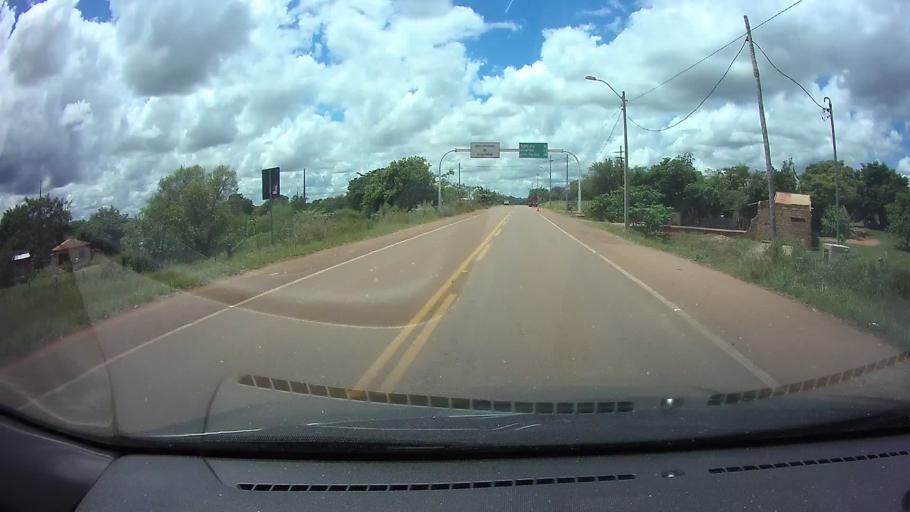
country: PY
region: Paraguari
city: La Colmena
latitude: -25.8930
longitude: -56.8421
